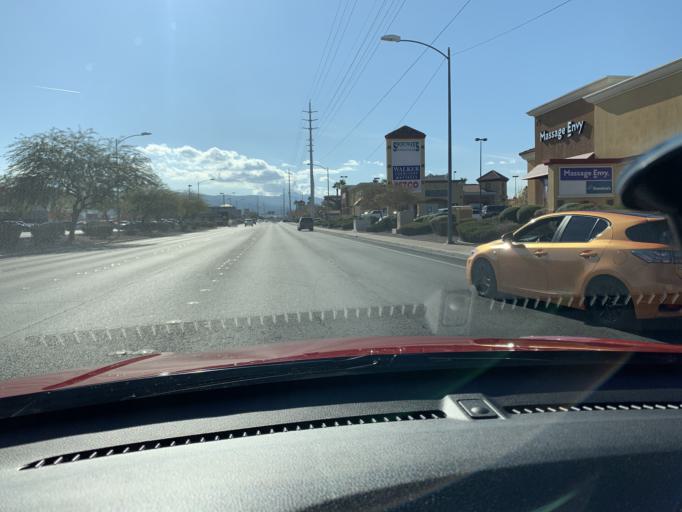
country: US
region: Nevada
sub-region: Clark County
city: Whitney
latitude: 36.0680
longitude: -115.0363
